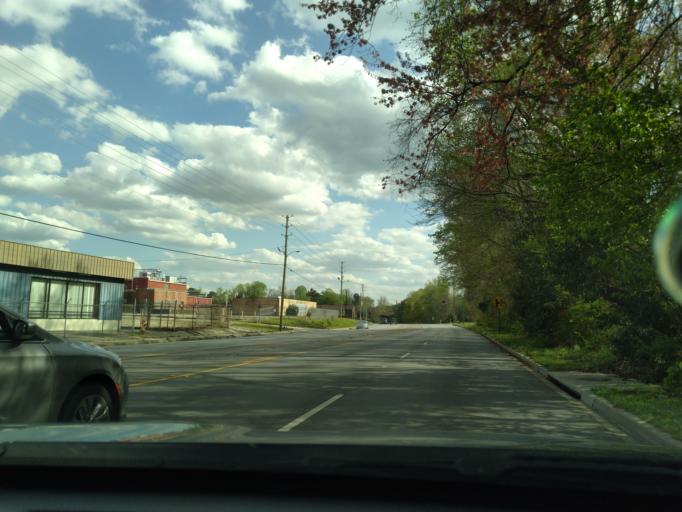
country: US
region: South Carolina
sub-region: Florence County
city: Florence
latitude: 34.1781
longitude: -79.7616
